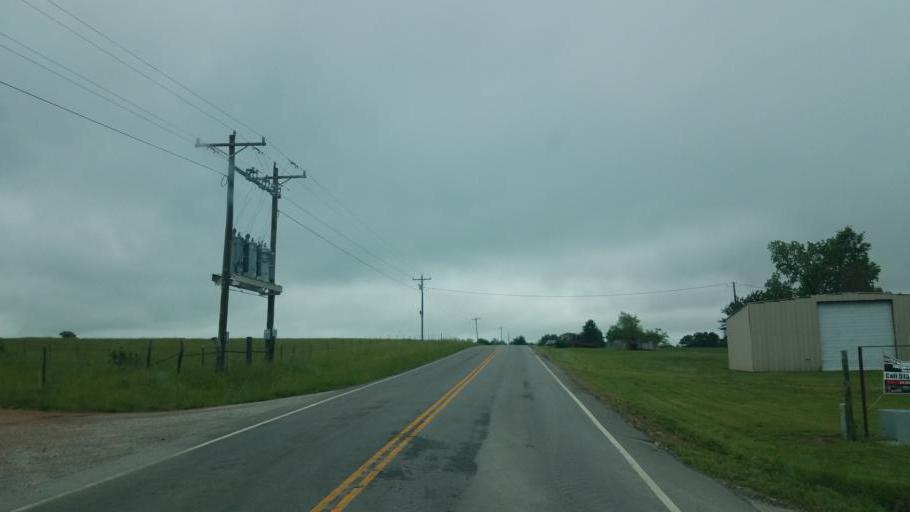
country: US
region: Missouri
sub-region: Moniteau County
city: California
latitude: 38.5250
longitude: -92.5735
